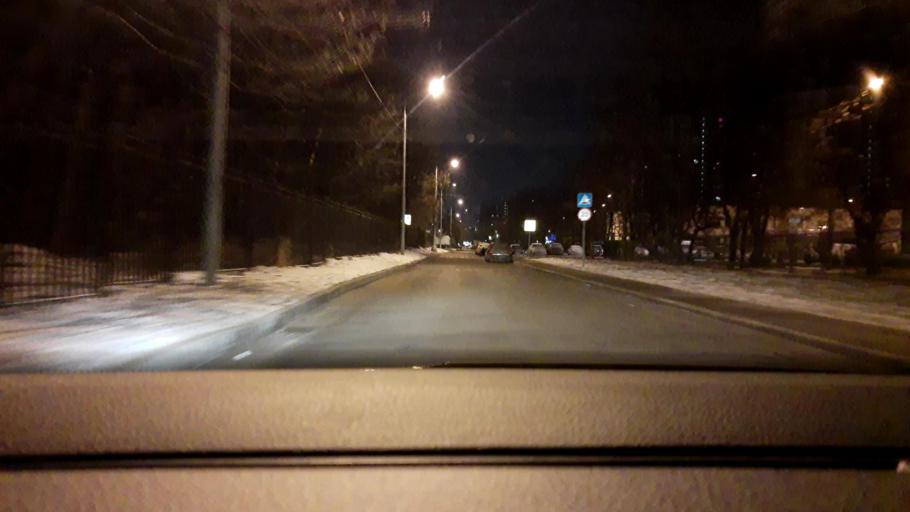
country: RU
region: Moscow
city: Lianozovo
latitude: 55.9019
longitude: 37.5915
